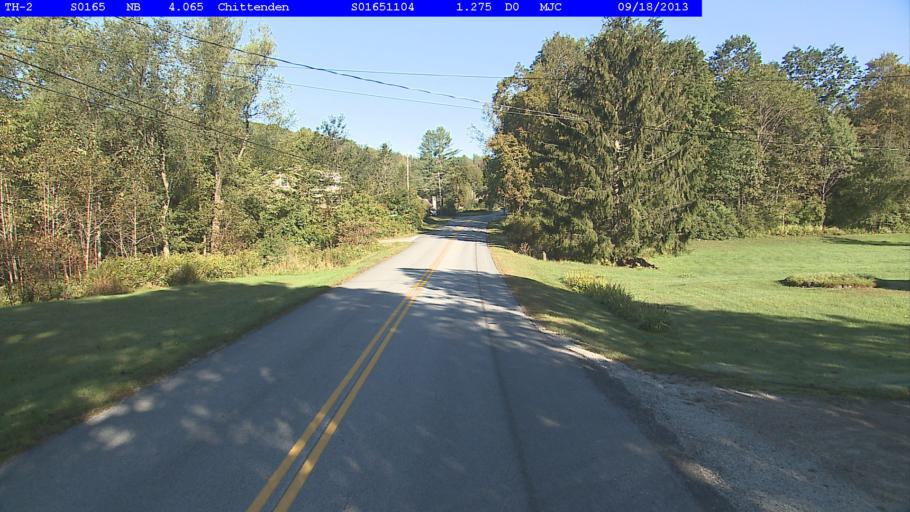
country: US
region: Vermont
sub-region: Rutland County
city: Rutland
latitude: 43.6946
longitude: -72.9555
